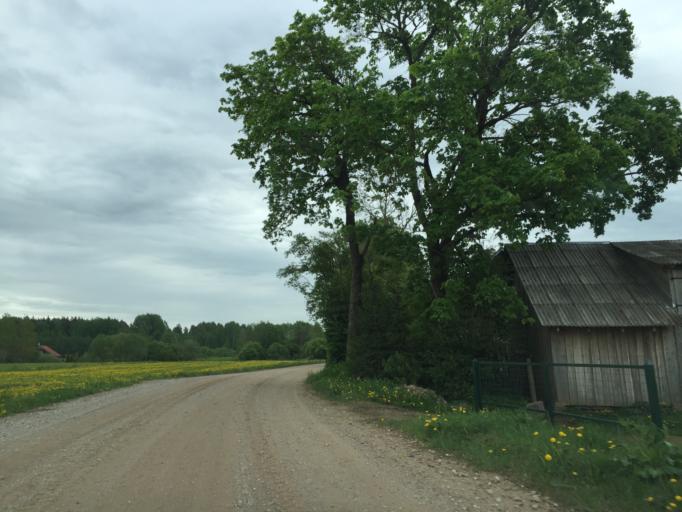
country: LV
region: Lielvarde
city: Lielvarde
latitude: 56.8063
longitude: 24.8376
